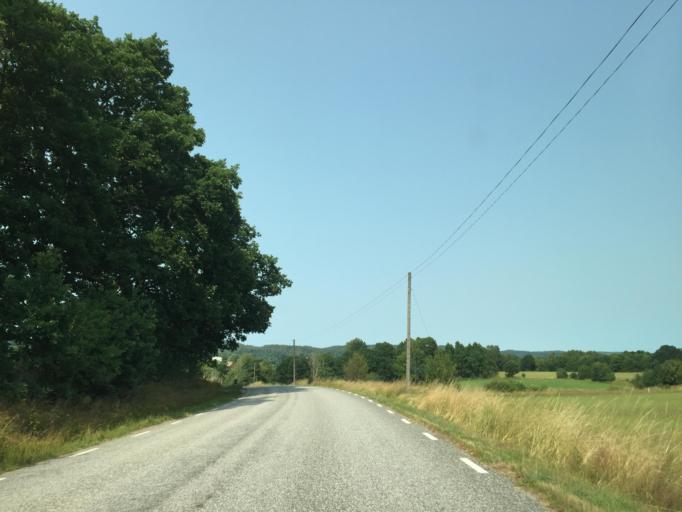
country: SE
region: Vaestra Goetaland
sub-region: Lilla Edets Kommun
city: Lilla Edet
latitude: 58.1844
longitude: 12.1175
